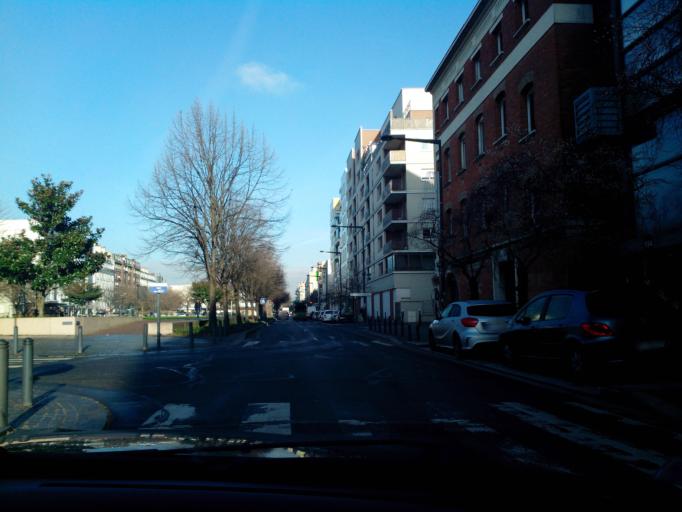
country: FR
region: Ile-de-France
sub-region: Departement de Seine-Saint-Denis
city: Saint-Denis
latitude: 48.9126
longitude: 2.3582
